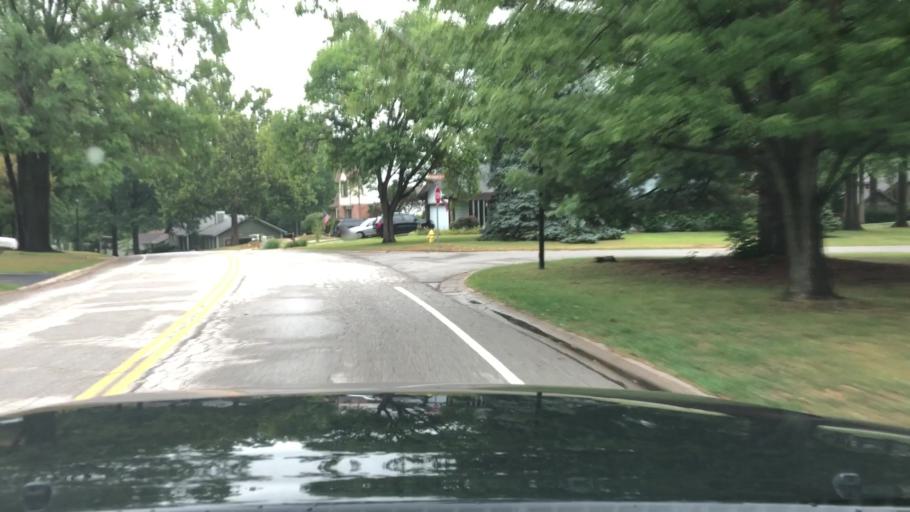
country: US
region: Missouri
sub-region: Saint Charles County
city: Lake Saint Louis
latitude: 38.7937
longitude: -90.7959
